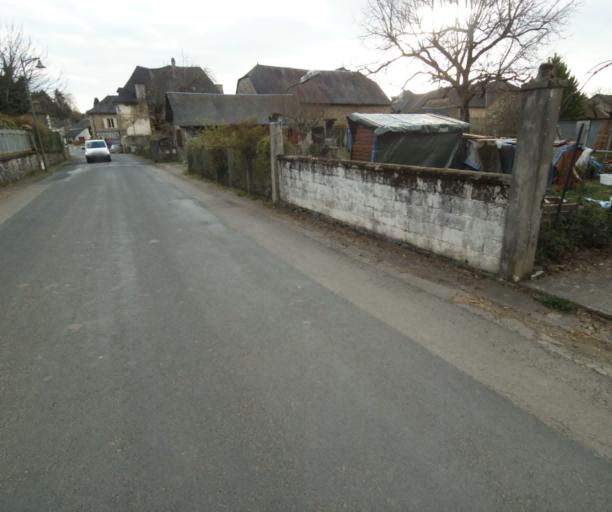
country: FR
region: Limousin
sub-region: Departement de la Correze
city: Saint-Clement
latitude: 45.3536
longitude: 1.6389
